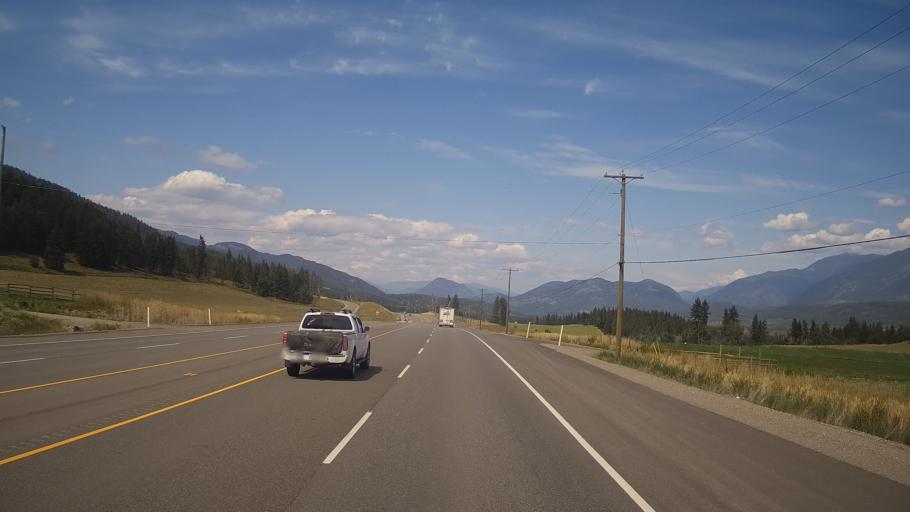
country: CA
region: British Columbia
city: Kamloops
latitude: 51.2827
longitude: -120.1780
